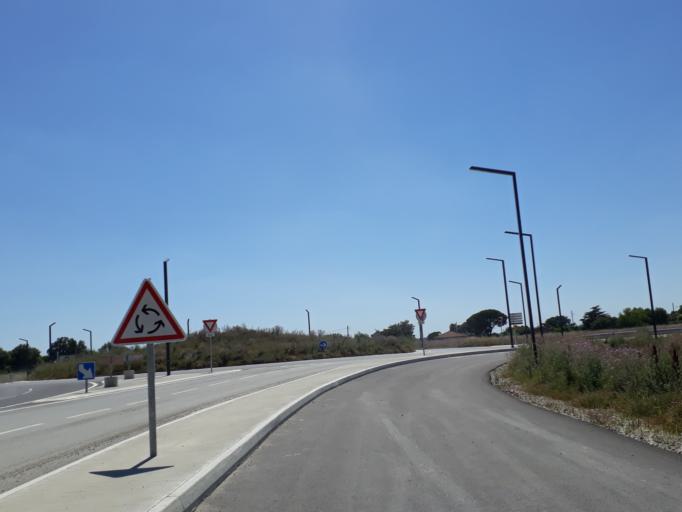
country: FR
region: Midi-Pyrenees
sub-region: Departement de la Haute-Garonne
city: Beauzelle
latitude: 43.6624
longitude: 1.3490
